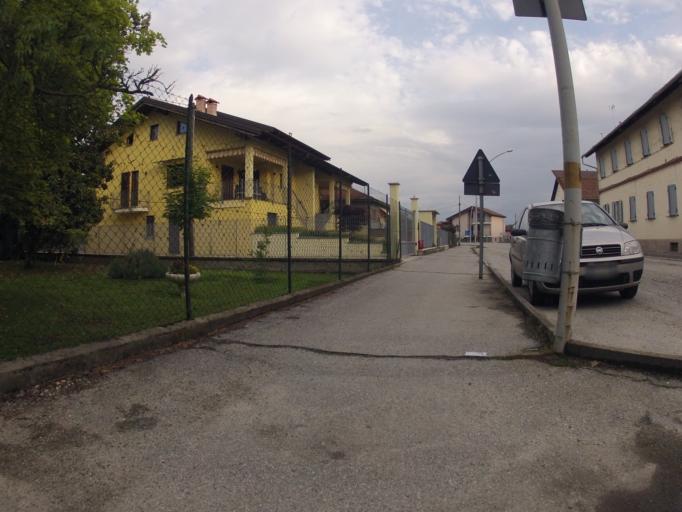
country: IT
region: Piedmont
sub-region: Provincia di Cuneo
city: Moretta
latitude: 44.7651
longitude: 7.5311
